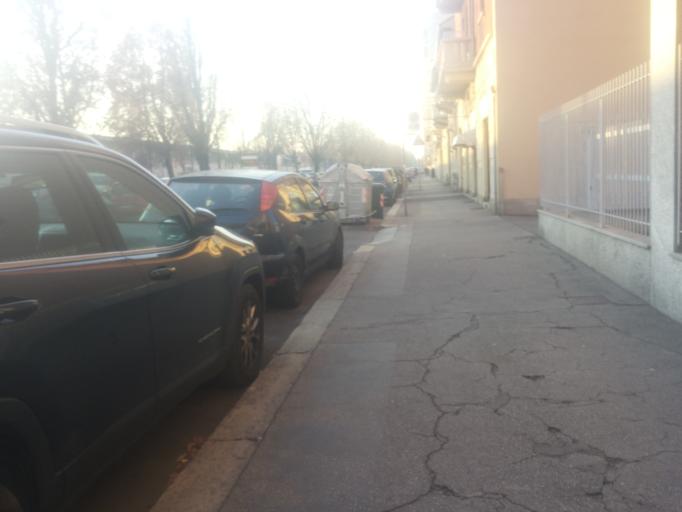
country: IT
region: Piedmont
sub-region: Provincia di Torino
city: Lesna
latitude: 45.0562
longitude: 7.6430
